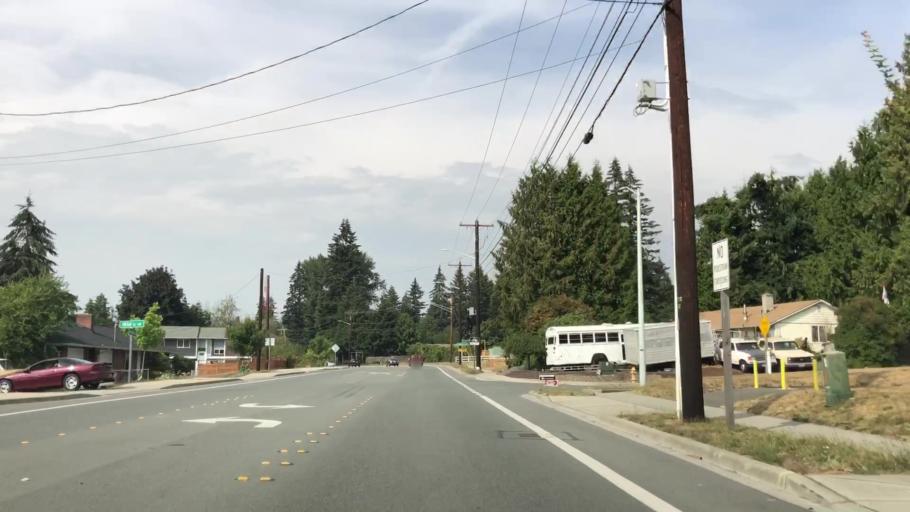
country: US
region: Washington
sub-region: Snohomish County
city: Martha Lake
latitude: 47.8335
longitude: -122.2369
